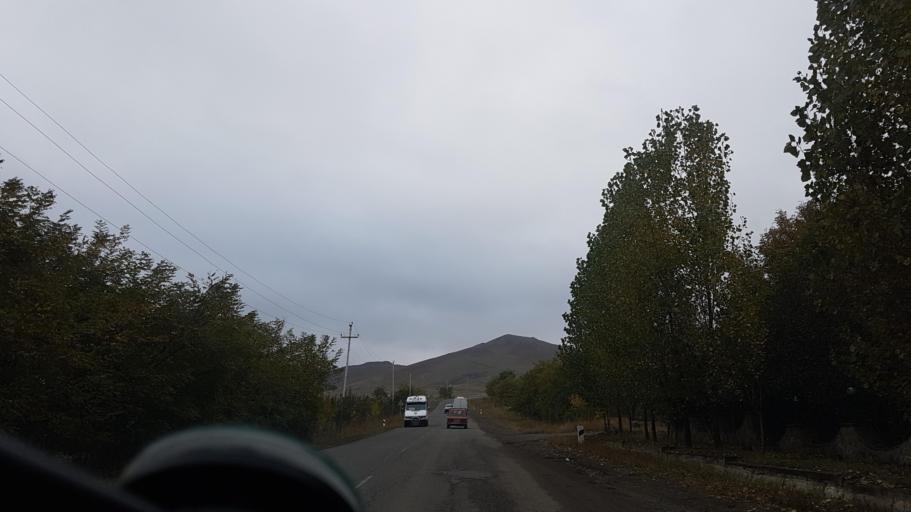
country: AZ
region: Gadabay Rayon
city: Ariqdam
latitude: 40.6292
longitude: 45.8148
